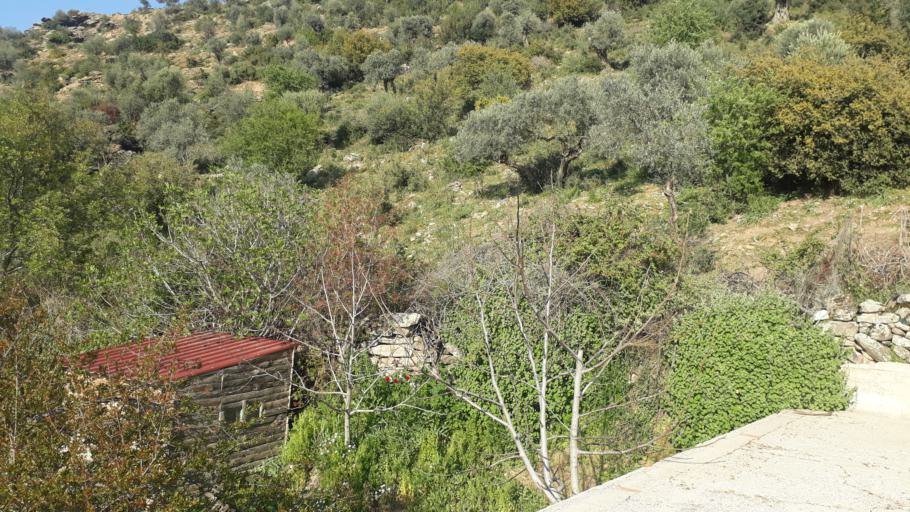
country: TR
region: Aydin
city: Bagarasi
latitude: 37.6687
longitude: 27.5222
